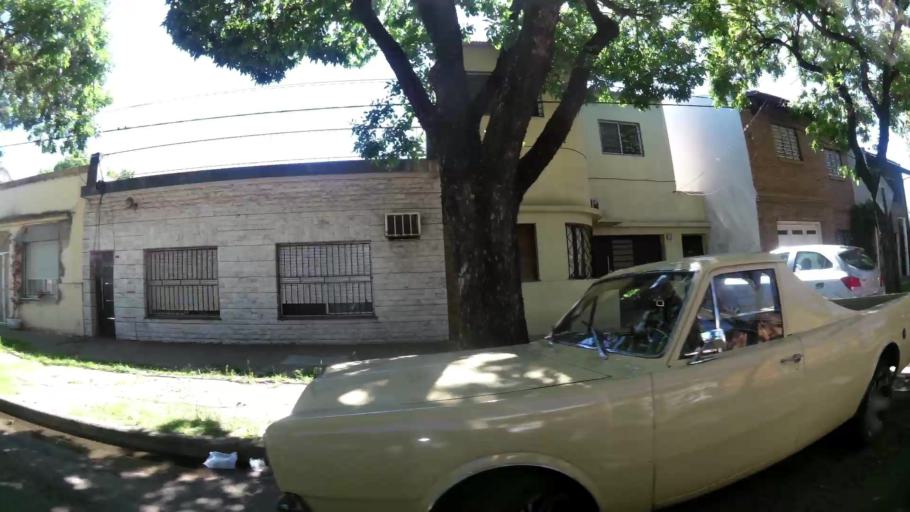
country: AR
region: Santa Fe
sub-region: Departamento de Rosario
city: Rosario
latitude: -32.9375
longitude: -60.6948
